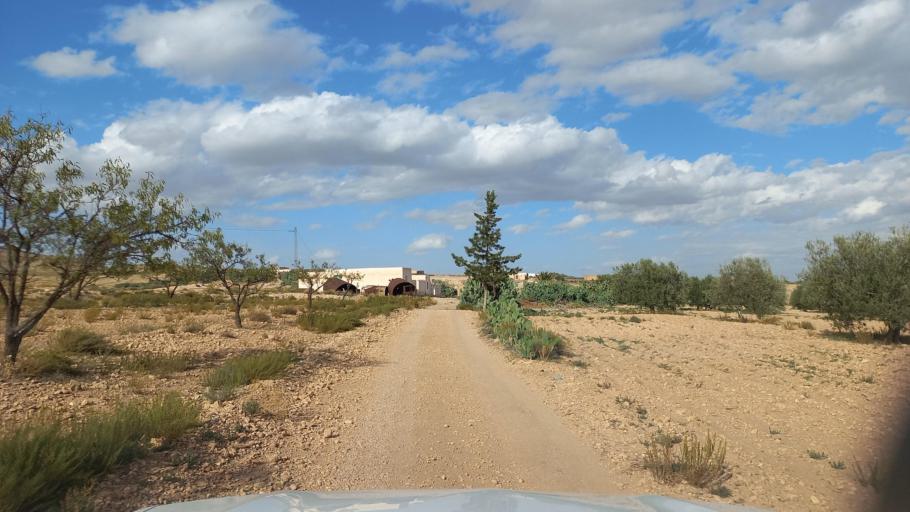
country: TN
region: Al Qasrayn
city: Sbiba
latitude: 35.4518
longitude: 9.0762
